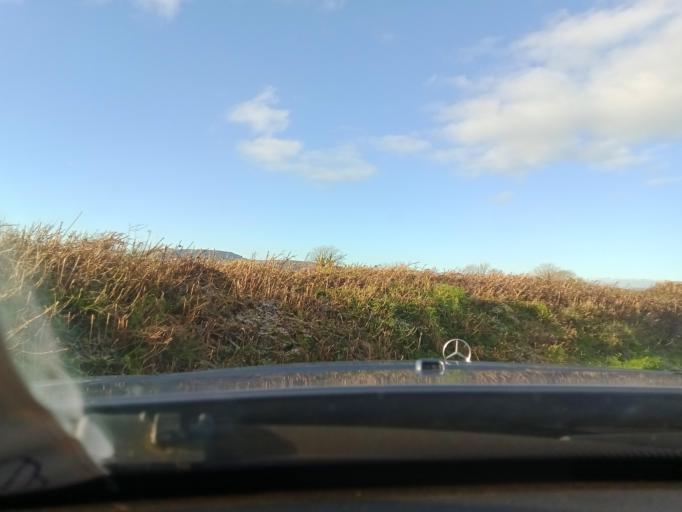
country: IE
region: Leinster
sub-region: Kilkenny
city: Graiguenamanagh
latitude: 52.5551
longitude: -6.9478
